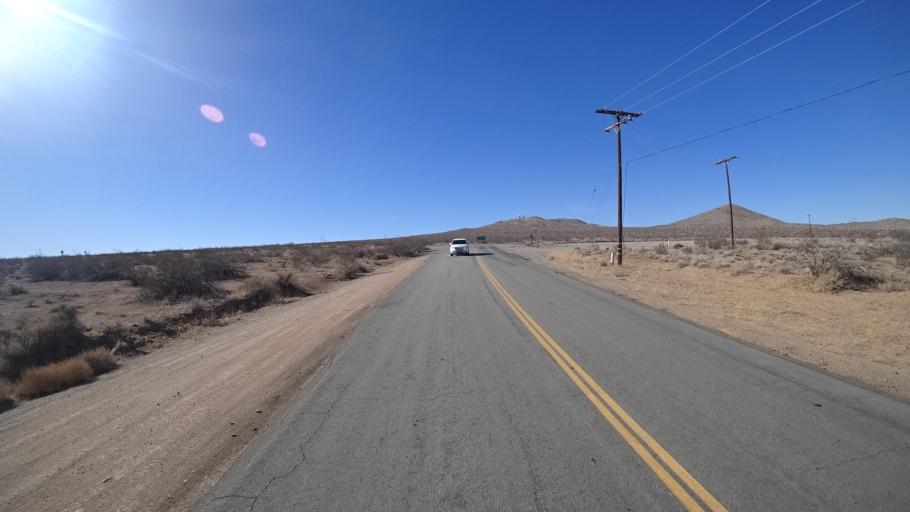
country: US
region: California
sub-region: Kern County
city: Ridgecrest
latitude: 35.4733
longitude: -117.6530
